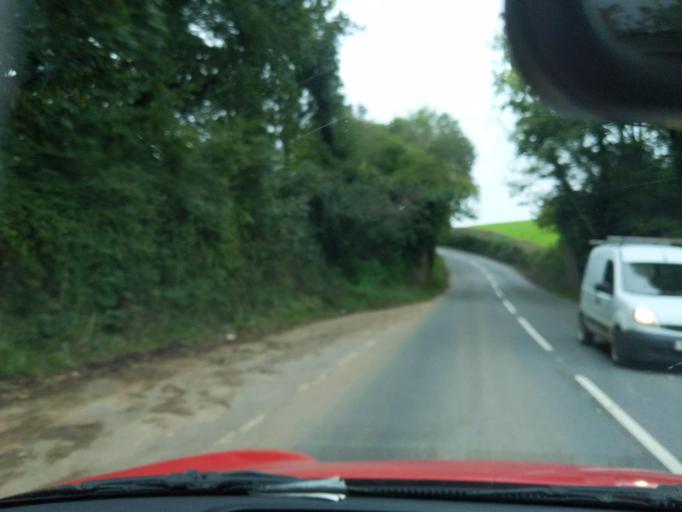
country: GB
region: England
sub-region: Devon
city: Okehampton
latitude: 50.8394
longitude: -4.0761
